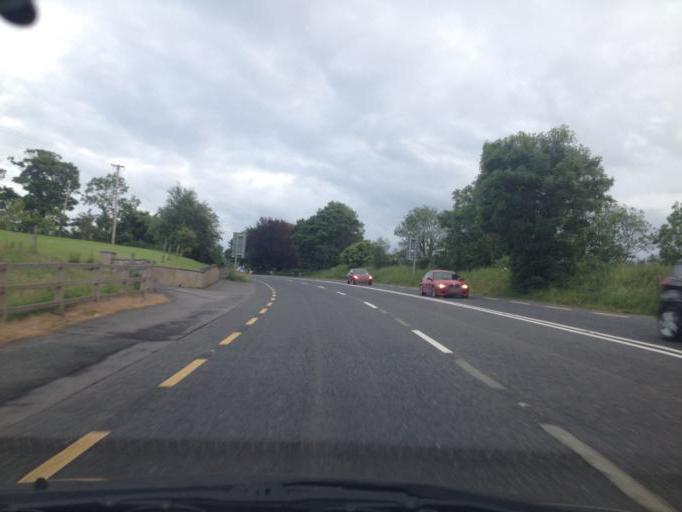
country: IE
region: Connaught
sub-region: Sligo
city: Strandhill
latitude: 54.3869
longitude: -8.5307
